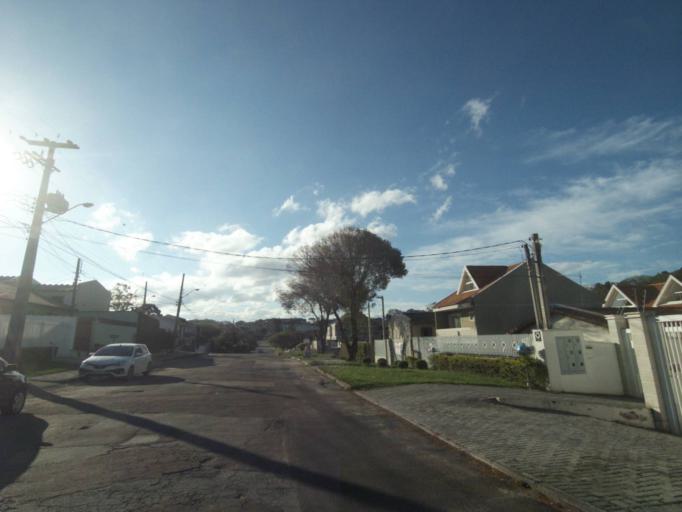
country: BR
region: Parana
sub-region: Curitiba
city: Curitiba
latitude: -25.3803
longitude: -49.2521
